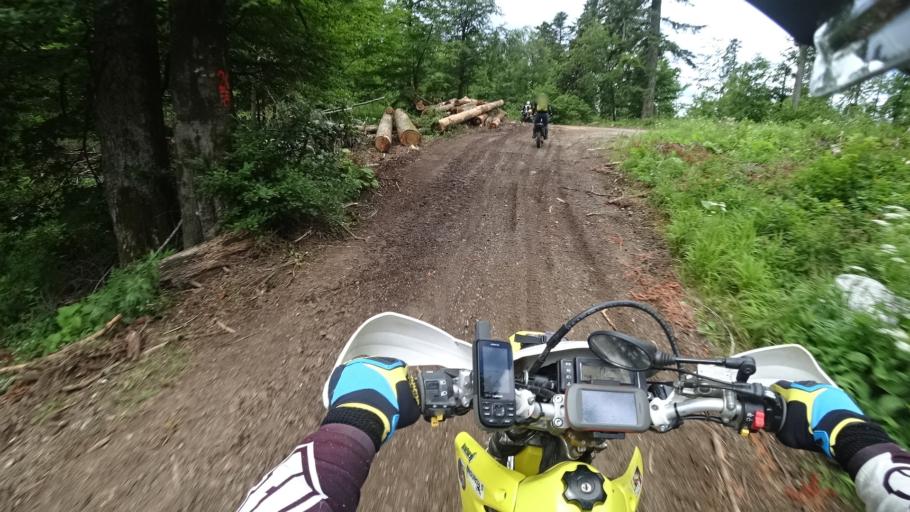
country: HR
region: Primorsko-Goranska
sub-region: Grad Delnice
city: Delnice
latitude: 45.3065
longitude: 14.7535
